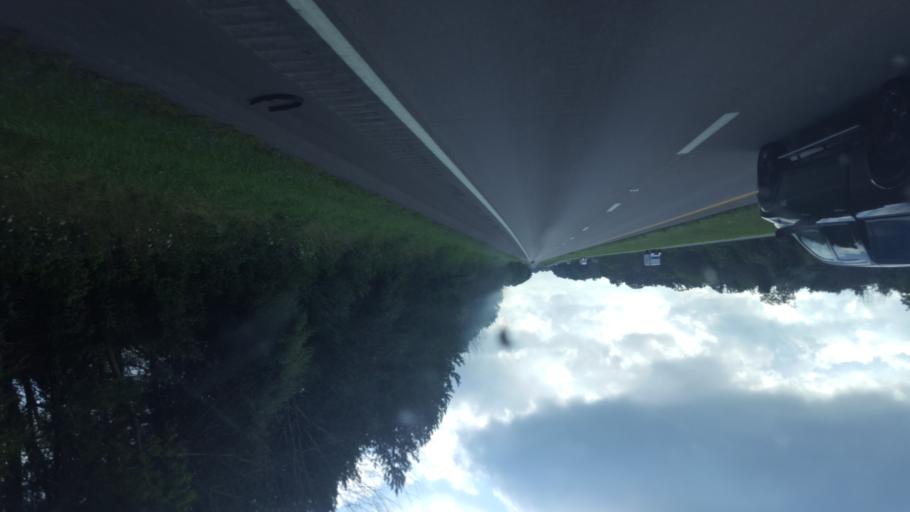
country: US
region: Ohio
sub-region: Wayne County
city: Dalton
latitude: 40.7862
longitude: -81.6169
